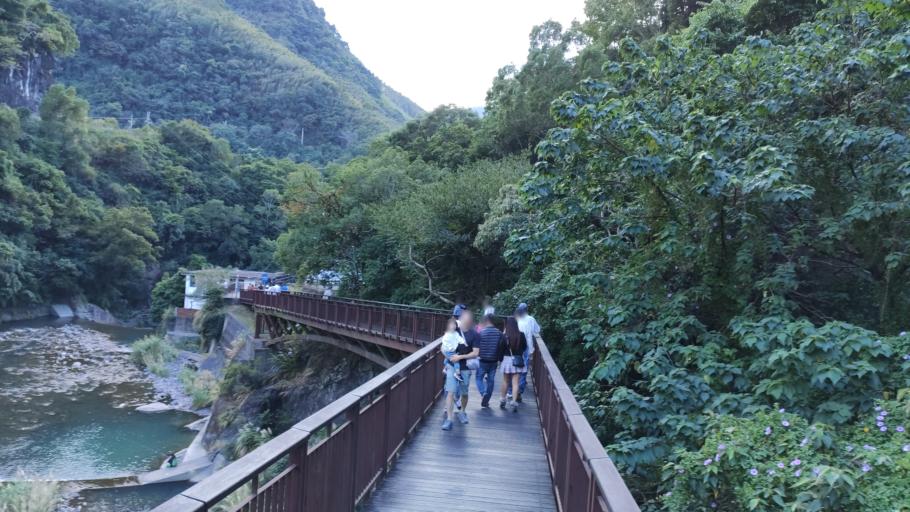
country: TW
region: Taiwan
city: Daxi
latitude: 24.7910
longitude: 121.3764
